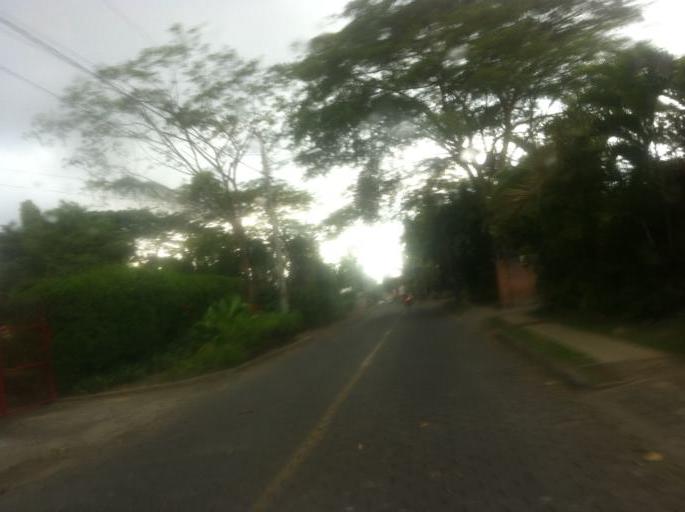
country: NI
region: Managua
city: Managua
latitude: 12.0945
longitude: -86.2347
